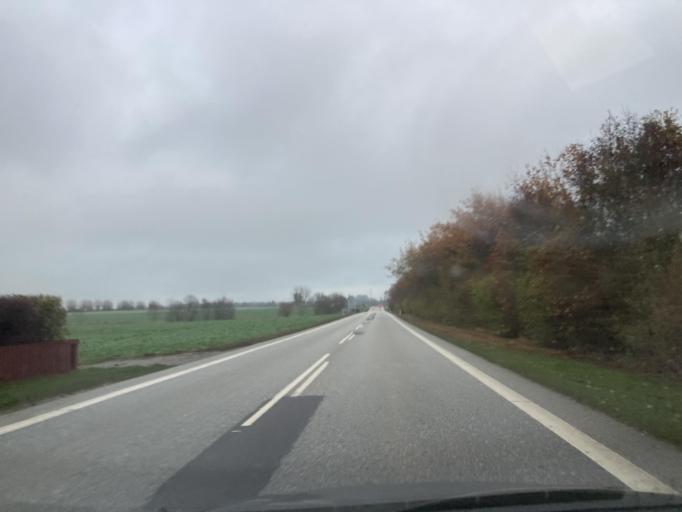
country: DK
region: Zealand
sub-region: Lolland Kommune
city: Holeby
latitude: 54.7156
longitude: 11.4339
